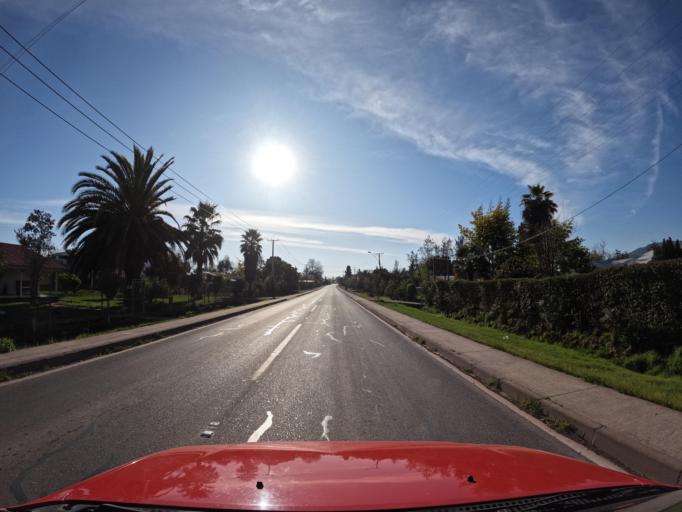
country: CL
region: Maule
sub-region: Provincia de Curico
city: Teno
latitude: -34.9549
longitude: -70.9791
